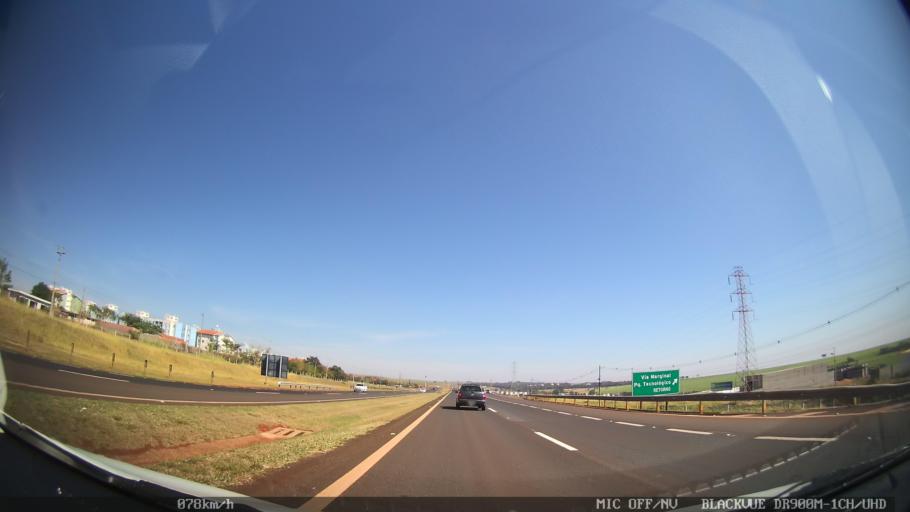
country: BR
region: Sao Paulo
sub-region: Ribeirao Preto
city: Ribeirao Preto
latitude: -21.1317
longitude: -47.8530
